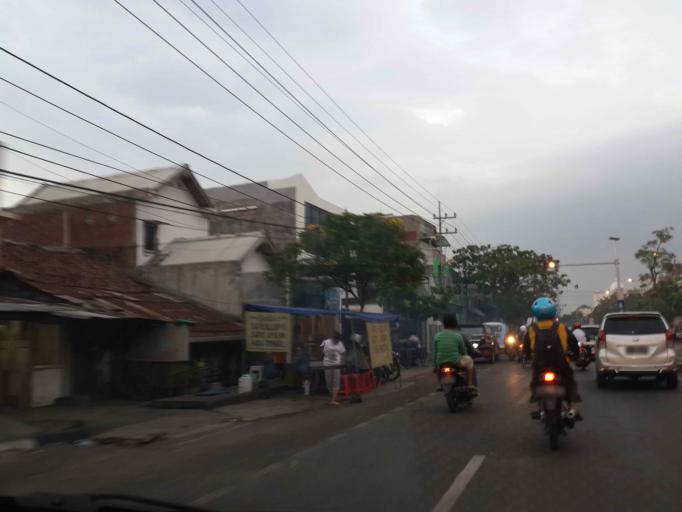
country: ID
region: East Java
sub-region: Kota Surabaya
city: Surabaya
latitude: -7.2555
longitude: 112.7250
